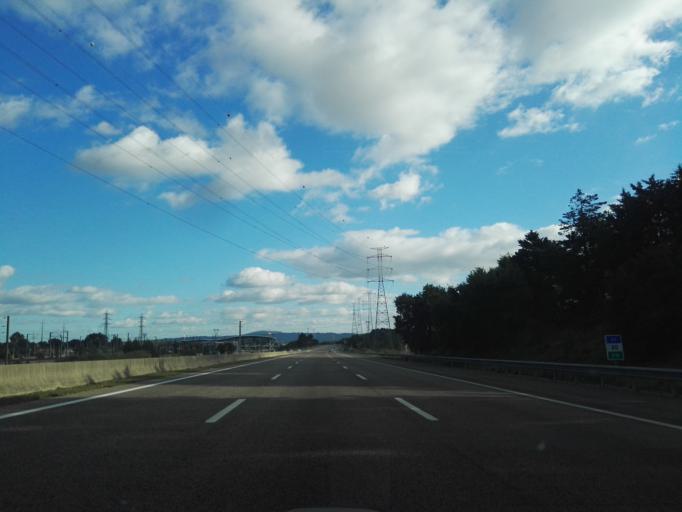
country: PT
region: Setubal
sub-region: Seixal
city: Aldeia de Paio Pires
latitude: 38.5874
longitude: -9.0581
